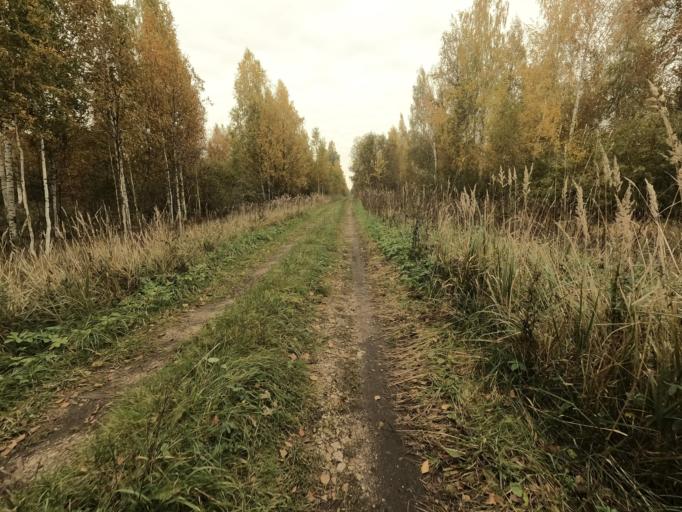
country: RU
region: Novgorod
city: Pankovka
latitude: 58.8809
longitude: 30.9433
